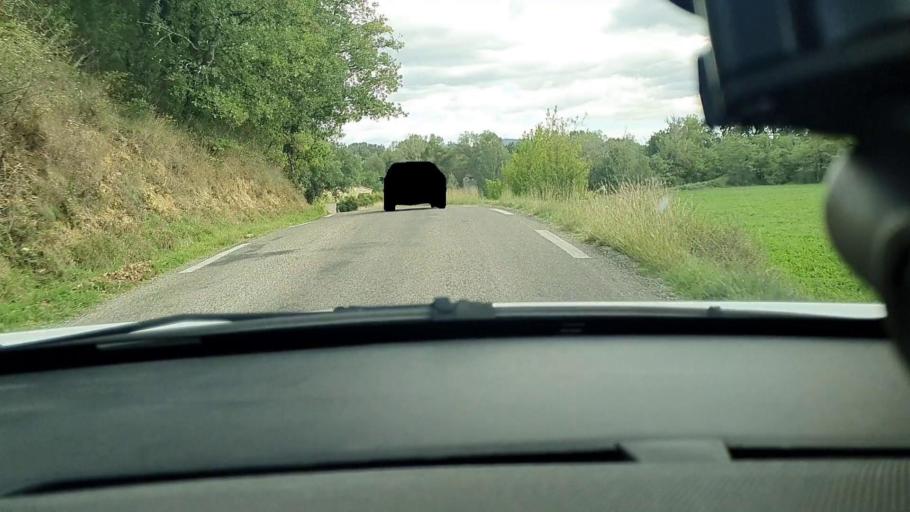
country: FR
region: Languedoc-Roussillon
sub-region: Departement du Gard
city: Les Mages
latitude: 44.2051
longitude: 4.2066
